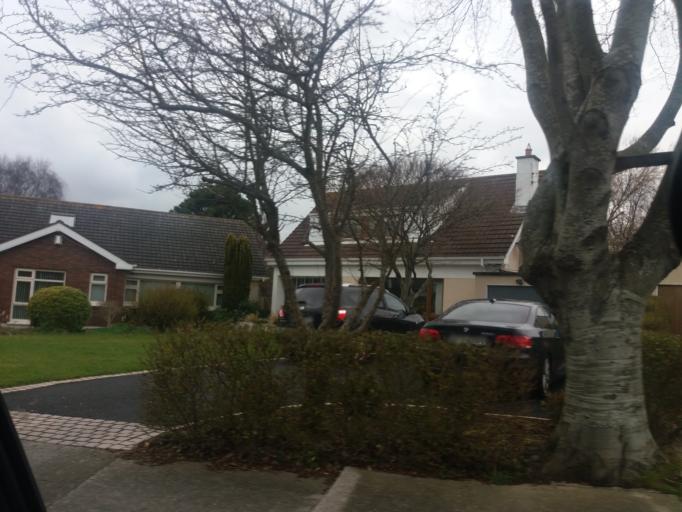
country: IE
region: Leinster
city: Sutton
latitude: 53.3838
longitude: -6.0963
